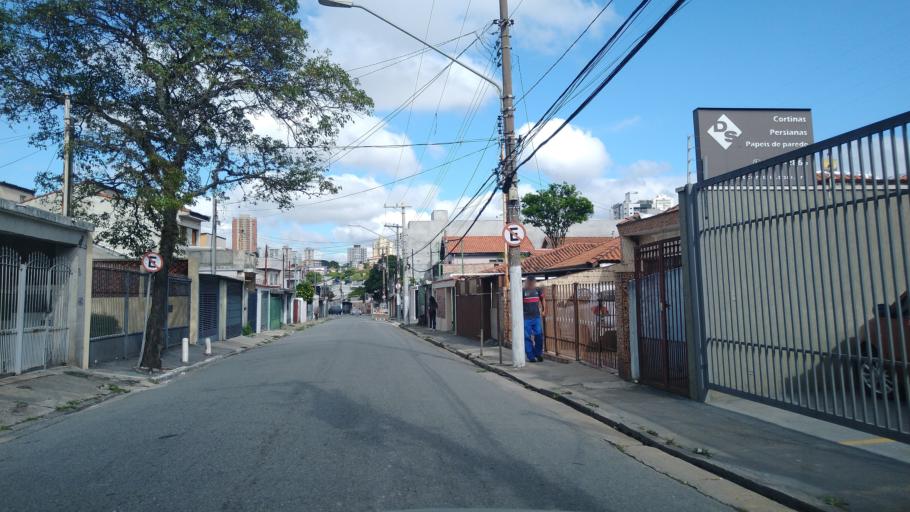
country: BR
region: Sao Paulo
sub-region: Sao Paulo
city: Sao Paulo
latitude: -23.4800
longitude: -46.6244
